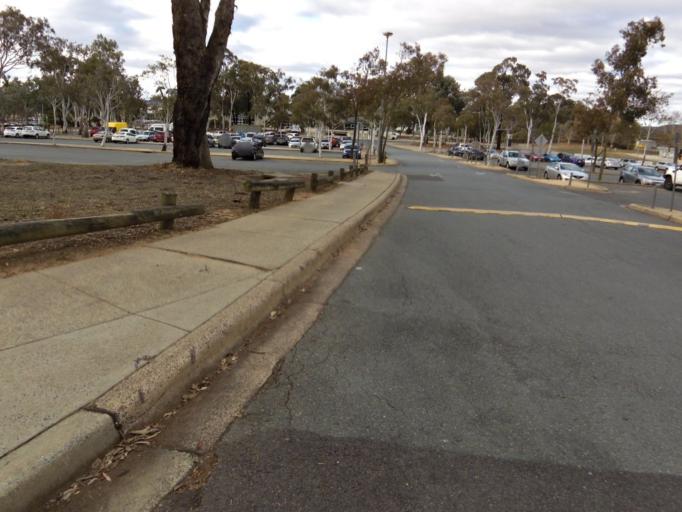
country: AU
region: Australian Capital Territory
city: Kaleen
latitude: -35.2495
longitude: 149.0997
